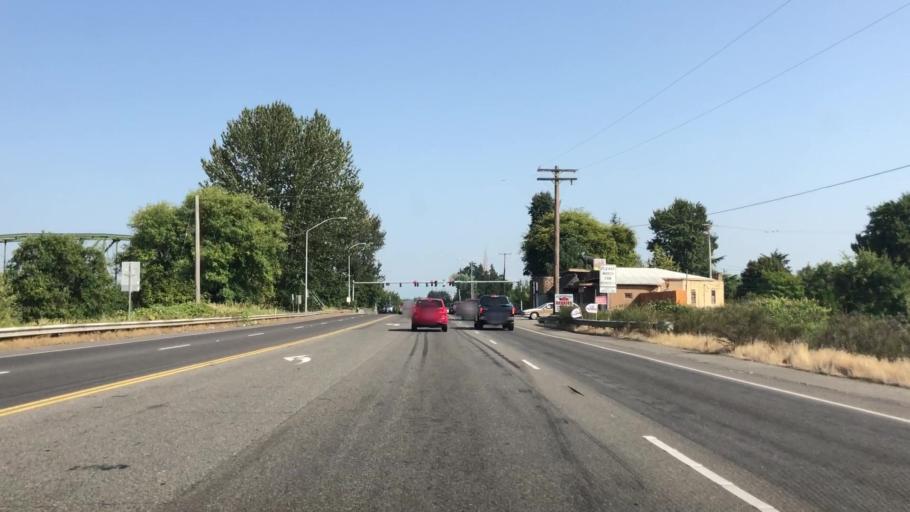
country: US
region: Washington
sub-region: Pierce County
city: Fife
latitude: 47.2144
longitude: -122.3436
